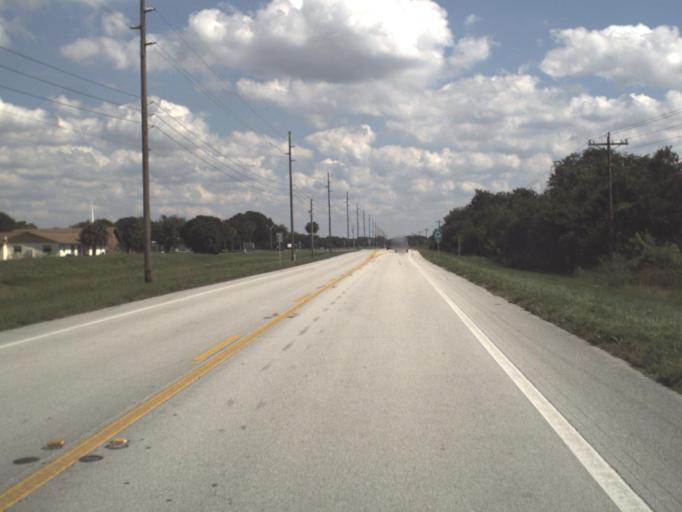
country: US
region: Florida
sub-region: Highlands County
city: Sebring
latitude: 27.4338
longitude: -81.3380
